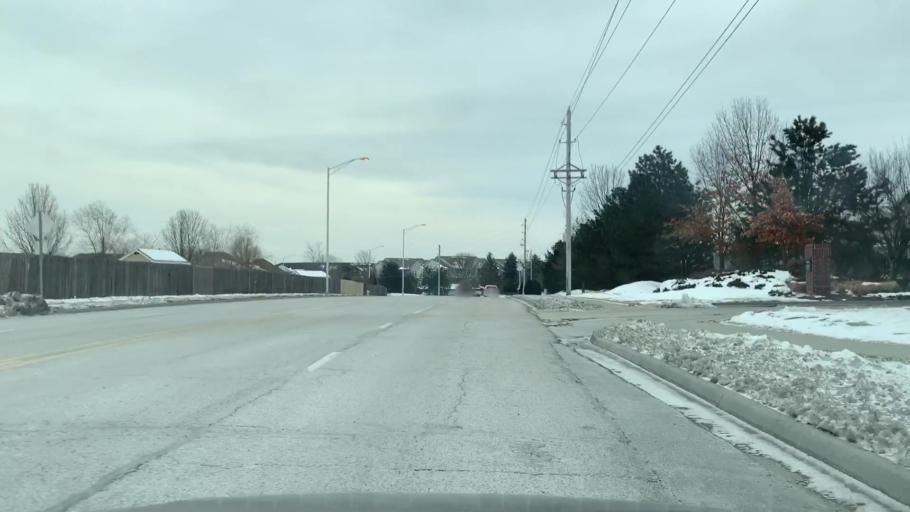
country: US
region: Missouri
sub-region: Jackson County
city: Lees Summit
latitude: 38.9304
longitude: -94.3703
